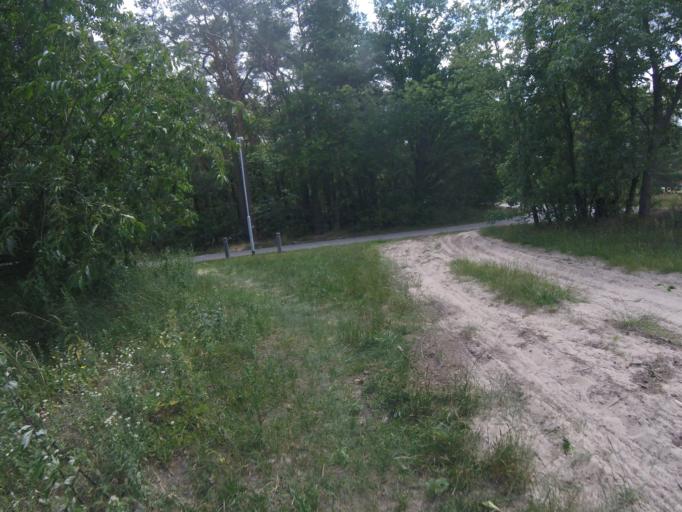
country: DE
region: Brandenburg
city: Bestensee
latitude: 52.2440
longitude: 13.6169
